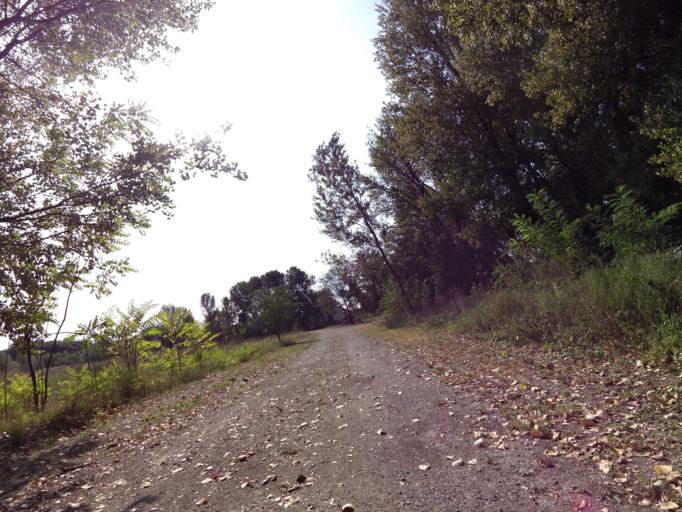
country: IT
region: Lombardy
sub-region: Citta metropolitana di Milano
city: Chiaravalle
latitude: 45.4294
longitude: 9.2313
